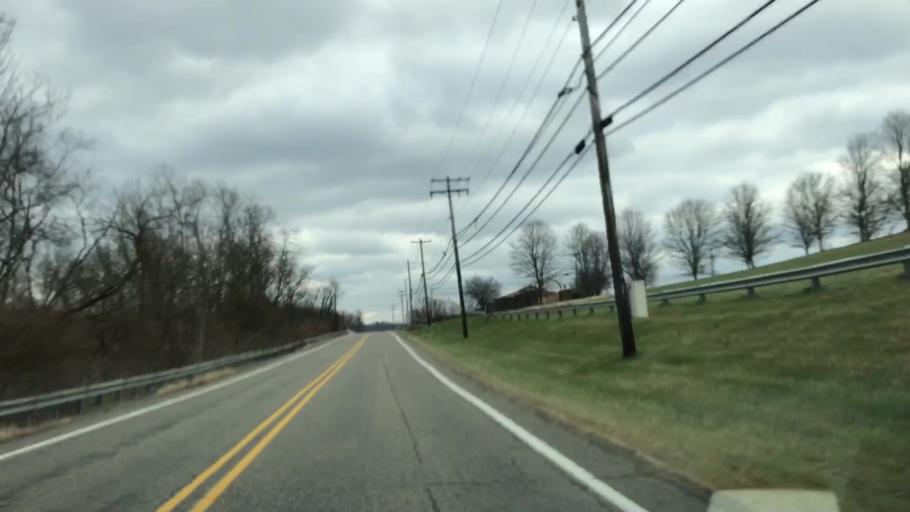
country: US
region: Pennsylvania
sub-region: Allegheny County
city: Heidelberg
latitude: 40.4060
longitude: -80.1095
